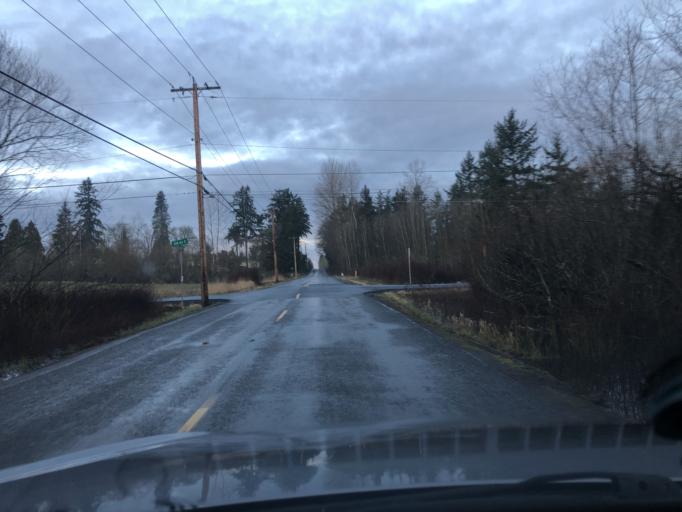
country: US
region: Washington
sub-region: Pierce County
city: North Puyallup
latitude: 47.2249
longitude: -122.2855
